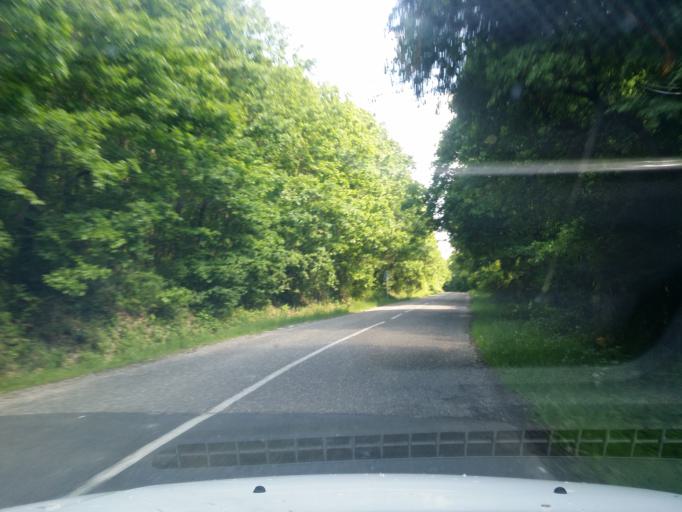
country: HU
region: Pest
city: Szob
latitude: 47.8567
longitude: 18.9093
